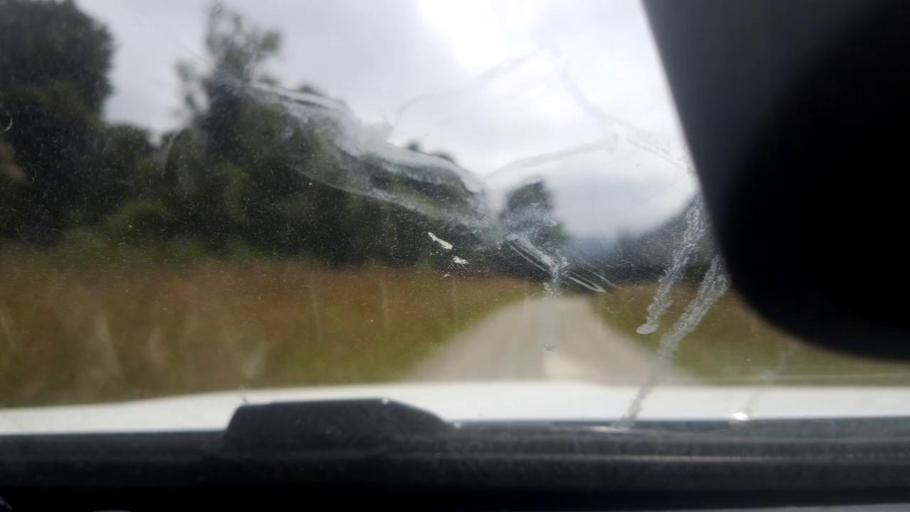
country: NZ
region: Canterbury
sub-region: Timaru District
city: Pleasant Point
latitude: -44.1405
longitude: 171.0832
